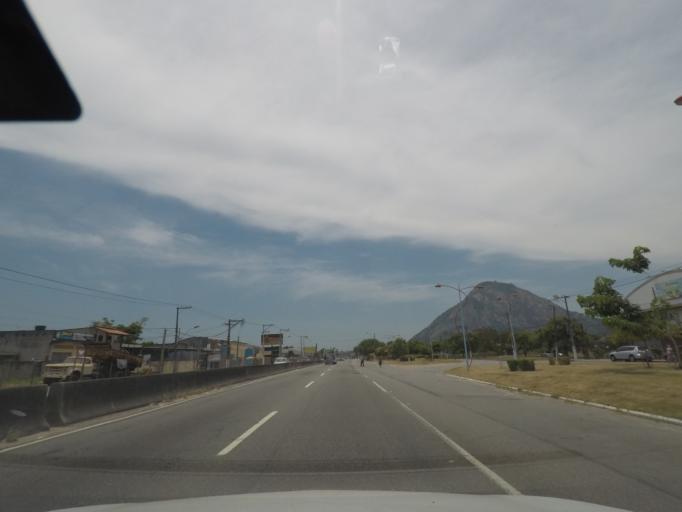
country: BR
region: Rio de Janeiro
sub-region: Marica
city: Marica
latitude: -22.9322
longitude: -42.8865
